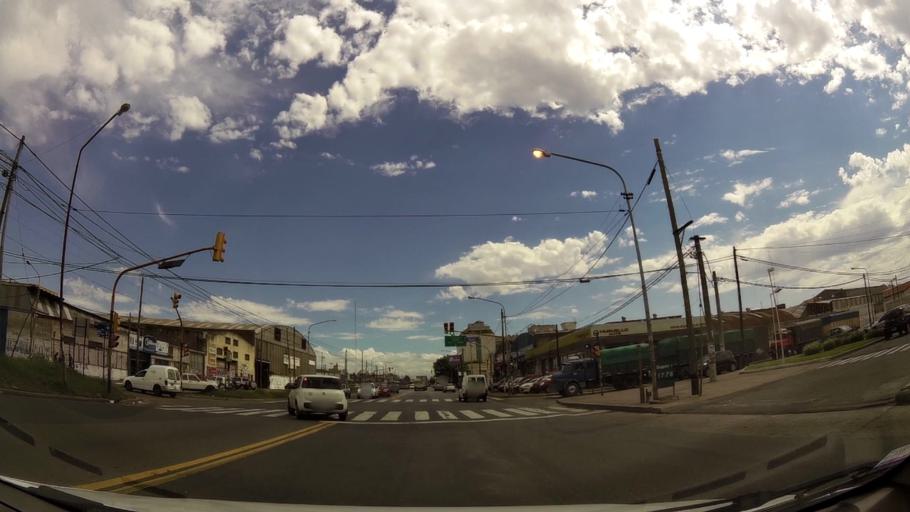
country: AR
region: Buenos Aires
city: San Justo
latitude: -34.6796
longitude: -58.5505
